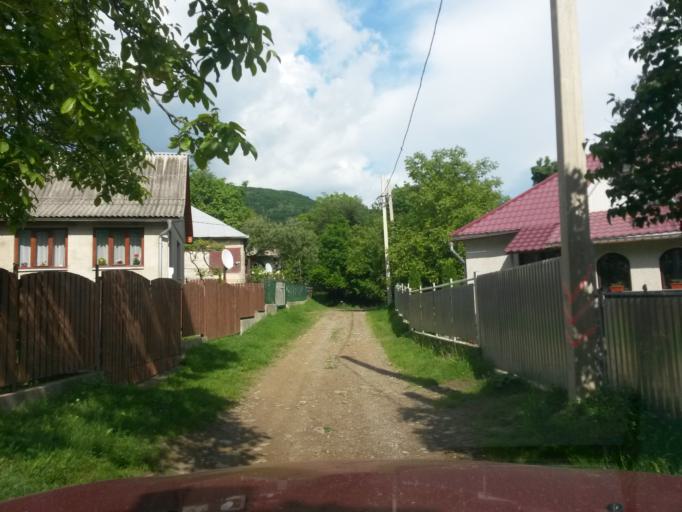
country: UA
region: Zakarpattia
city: Velykyi Bereznyi
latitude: 48.8987
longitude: 22.5282
